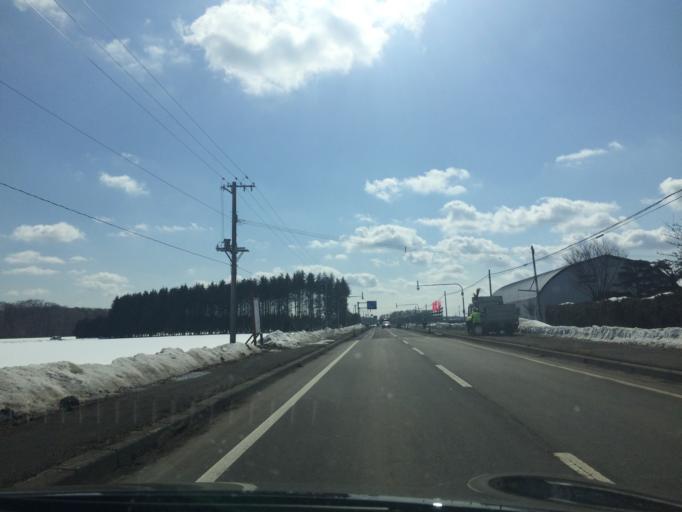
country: JP
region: Hokkaido
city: Chitose
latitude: 42.8737
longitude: 141.6310
